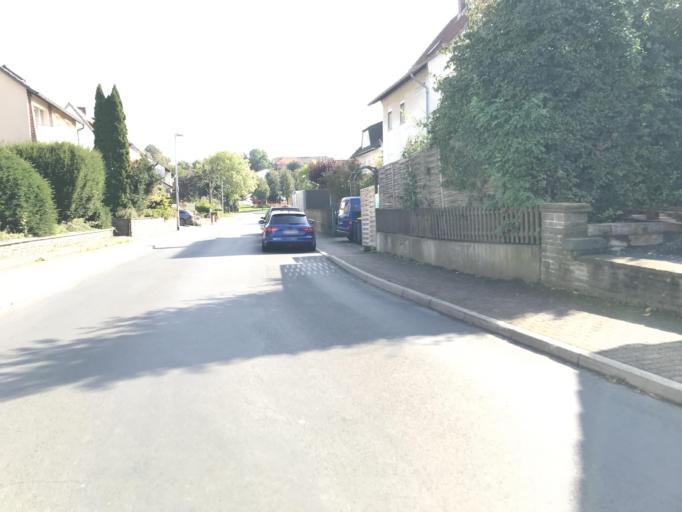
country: DE
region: Hesse
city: Gudensberg
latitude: 51.1666
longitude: 9.3748
